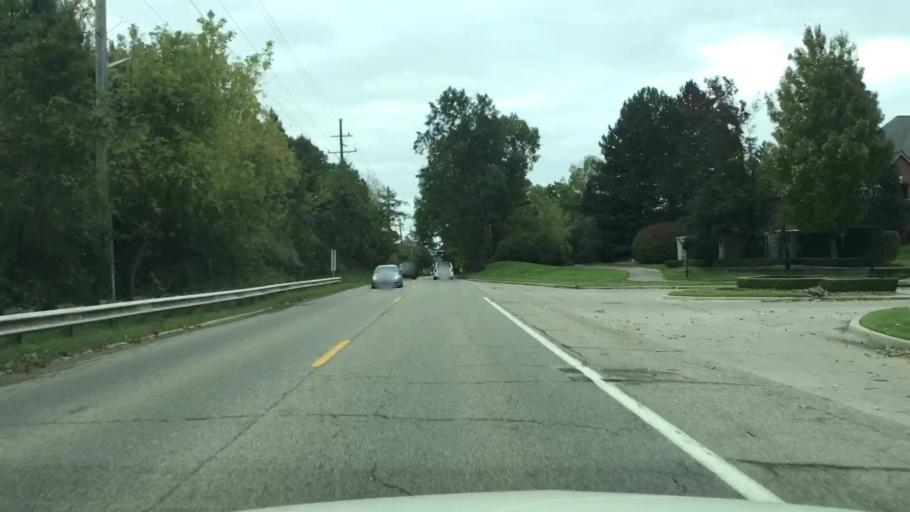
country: US
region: Michigan
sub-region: Macomb County
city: Shelby
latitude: 42.7170
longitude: -83.0561
